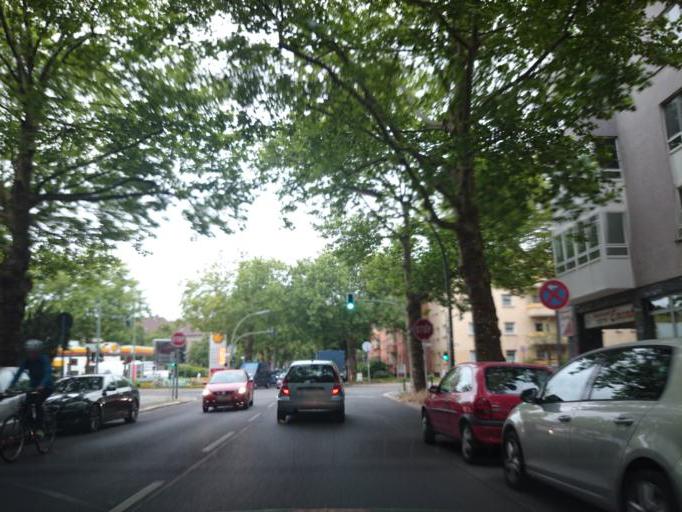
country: DE
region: Berlin
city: Steglitz Bezirk
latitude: 52.4587
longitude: 13.3399
